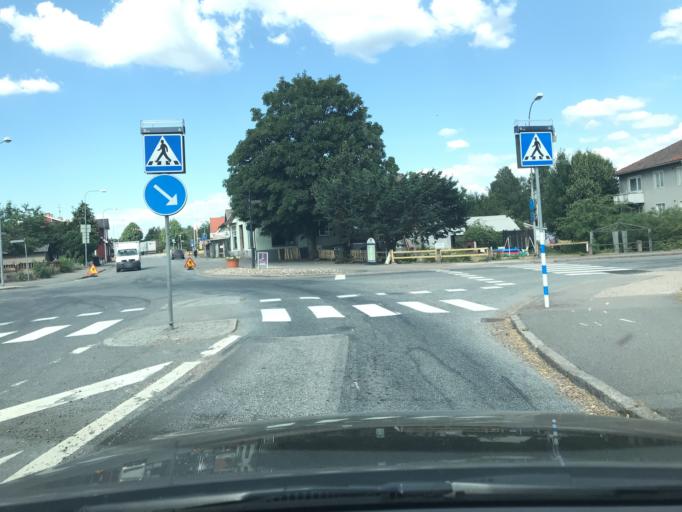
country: SE
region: Skane
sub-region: Hassleholms Kommun
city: Hastveda
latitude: 56.2840
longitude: 13.9352
